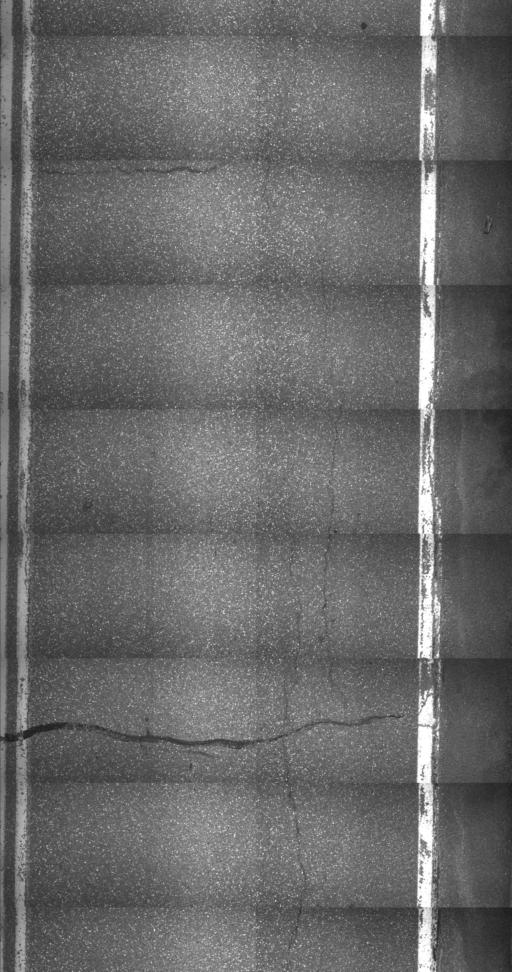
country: US
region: New Hampshire
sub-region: Grafton County
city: Woodsville
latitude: 44.2108
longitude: -72.2591
